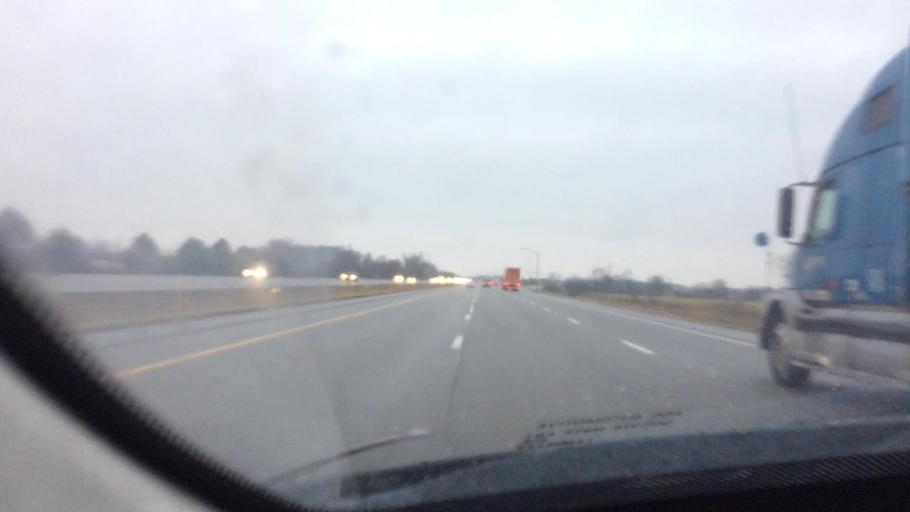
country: US
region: Ohio
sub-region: Wood County
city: Bowling Green
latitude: 41.2848
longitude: -83.6377
